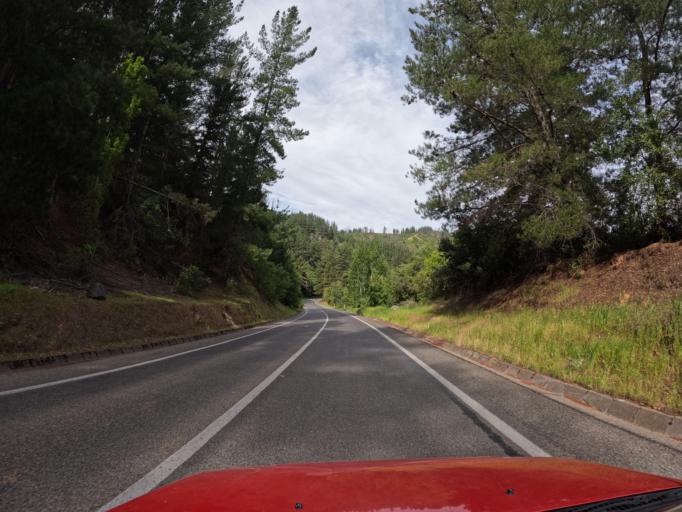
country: CL
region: Maule
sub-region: Provincia de Talca
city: Talca
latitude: -35.2974
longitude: -71.9659
